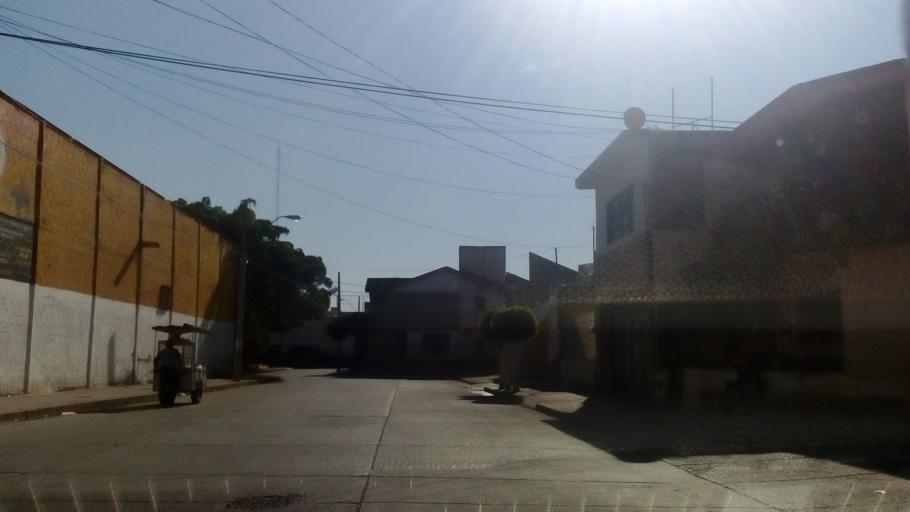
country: MX
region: Guanajuato
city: Leon
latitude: 21.1352
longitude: -101.6922
